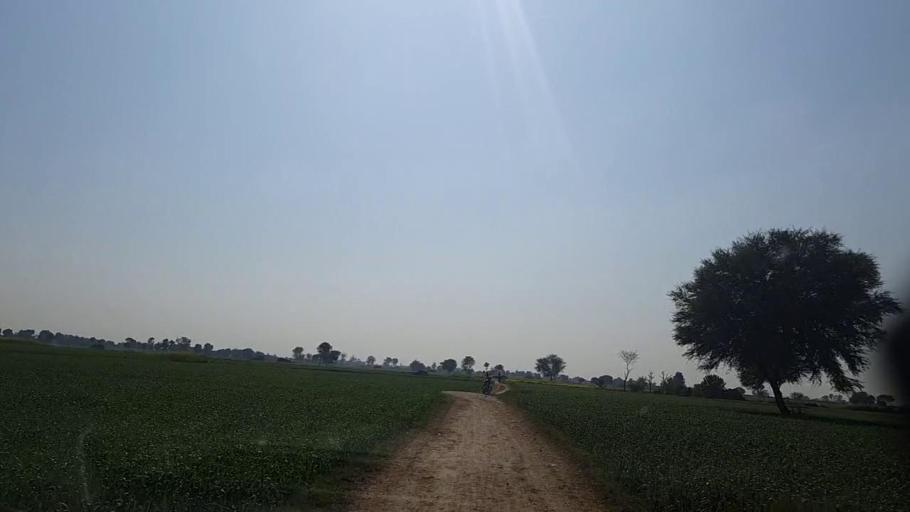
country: PK
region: Sindh
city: Sakrand
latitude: 26.1620
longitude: 68.3195
